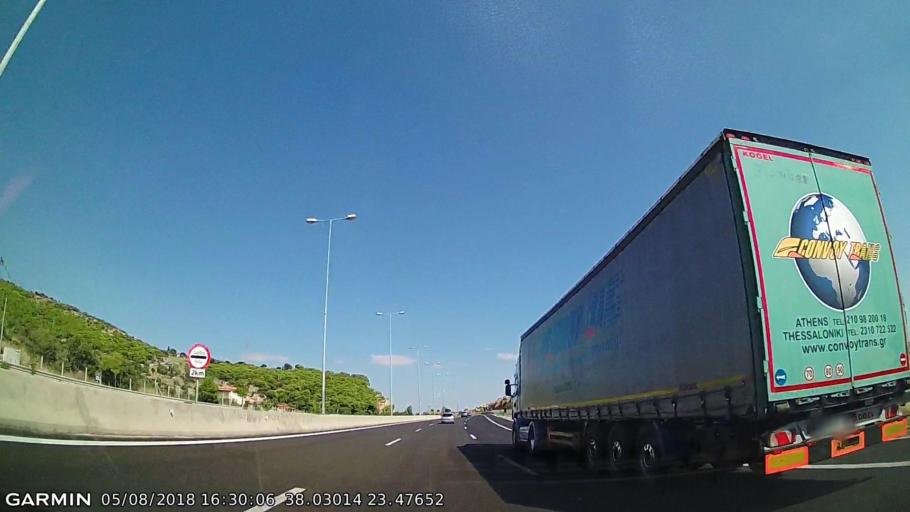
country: GR
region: Attica
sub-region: Nomarchia Dytikis Attikis
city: Vlychada
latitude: 38.0301
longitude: 23.4770
